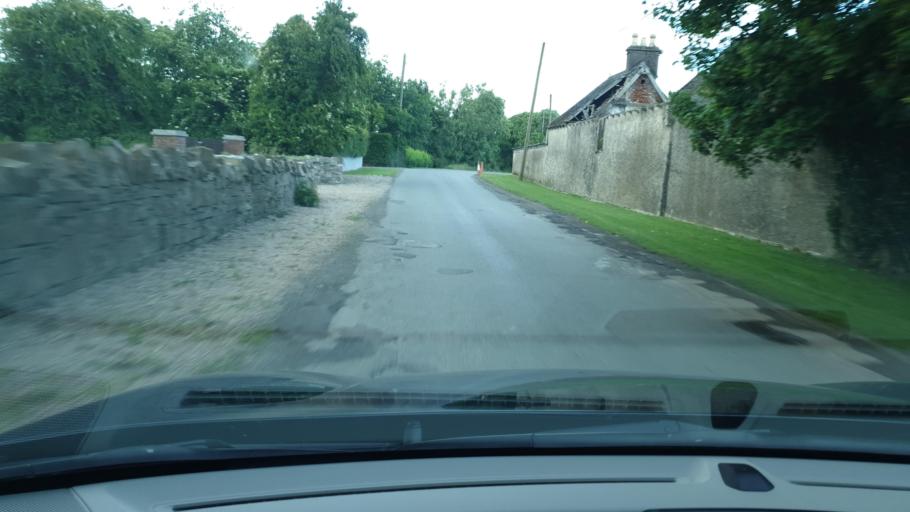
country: IE
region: Leinster
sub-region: An Mhi
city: Ratoath
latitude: 53.5594
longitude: -6.4974
